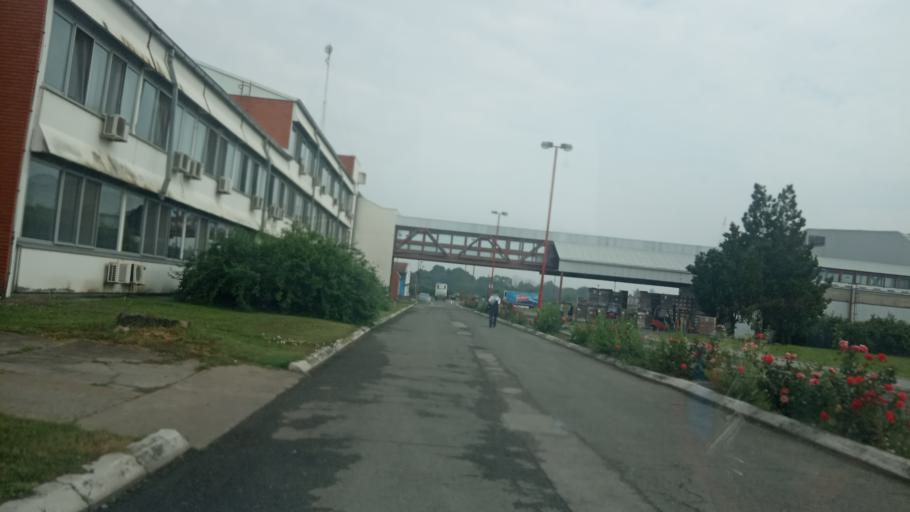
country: RS
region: Central Serbia
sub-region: Belgrade
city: Zemun
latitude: 44.9231
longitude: 20.4410
